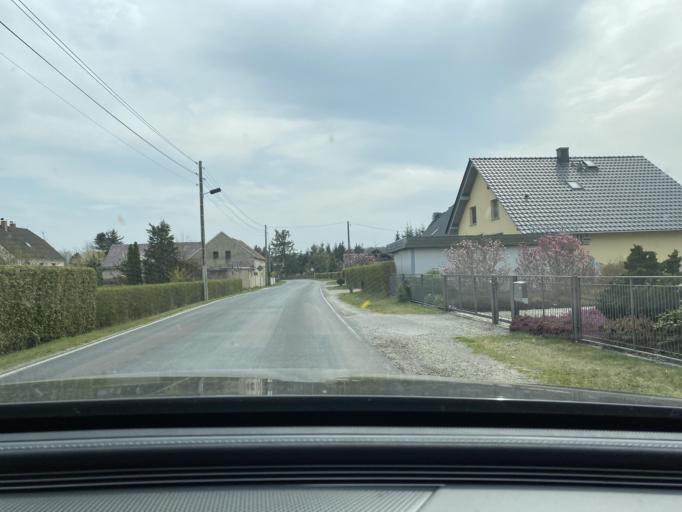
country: DE
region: Saxony
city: Neschwitz
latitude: 51.2863
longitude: 14.3193
